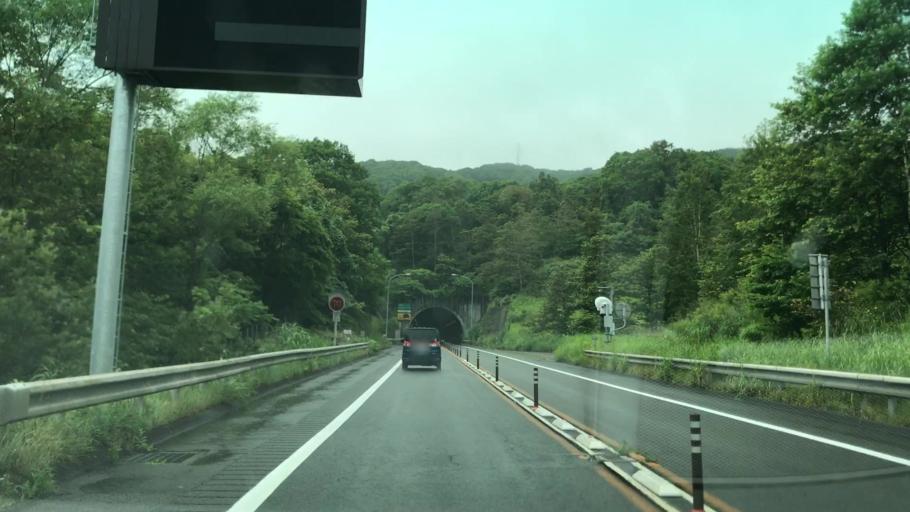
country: JP
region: Hokkaido
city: Muroran
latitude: 42.3900
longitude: 141.0594
